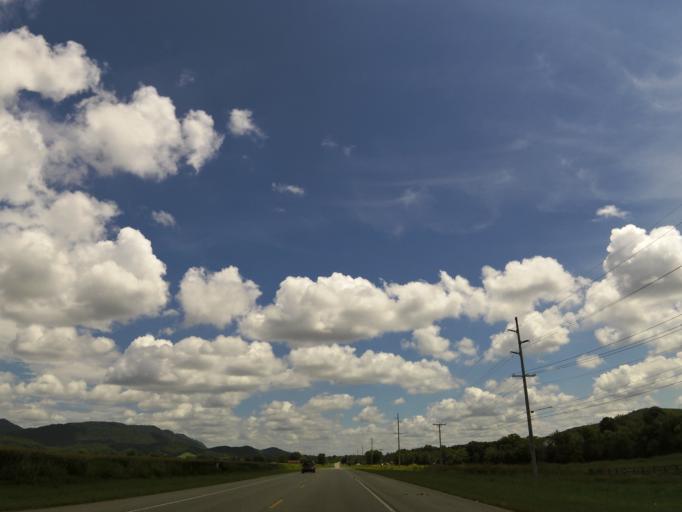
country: US
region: Kentucky
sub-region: Bell County
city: Middlesboro
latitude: 36.5195
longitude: -83.7609
